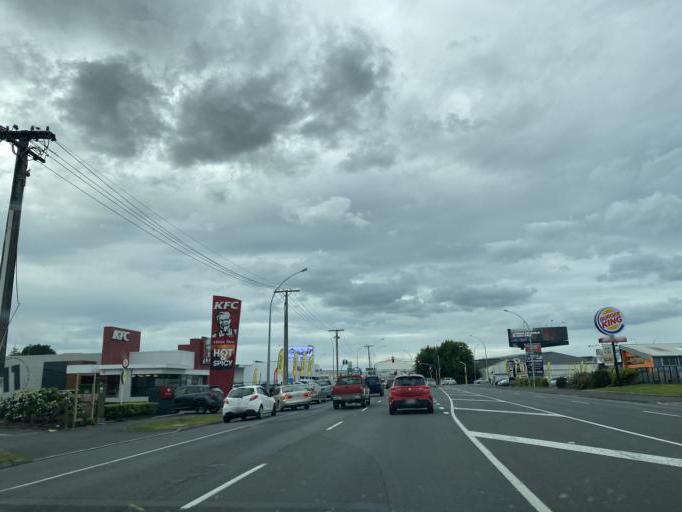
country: NZ
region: Waikato
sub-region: Hamilton City
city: Hamilton
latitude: -37.7904
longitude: 175.2599
